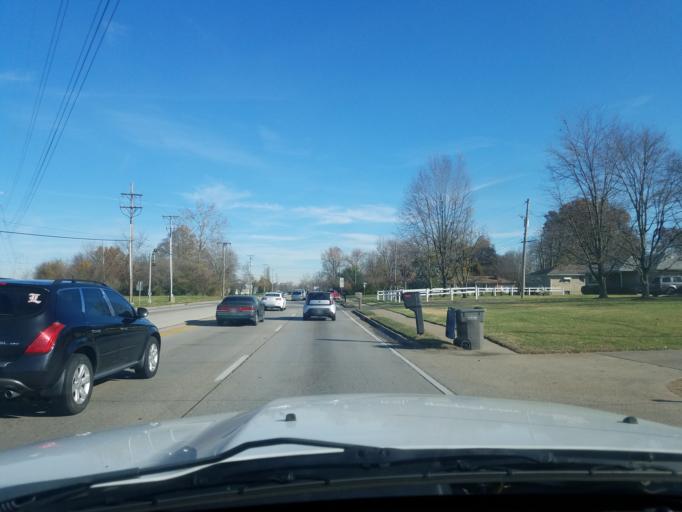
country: US
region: Kentucky
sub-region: Jefferson County
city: Saint Dennis
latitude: 38.1847
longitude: -85.8543
